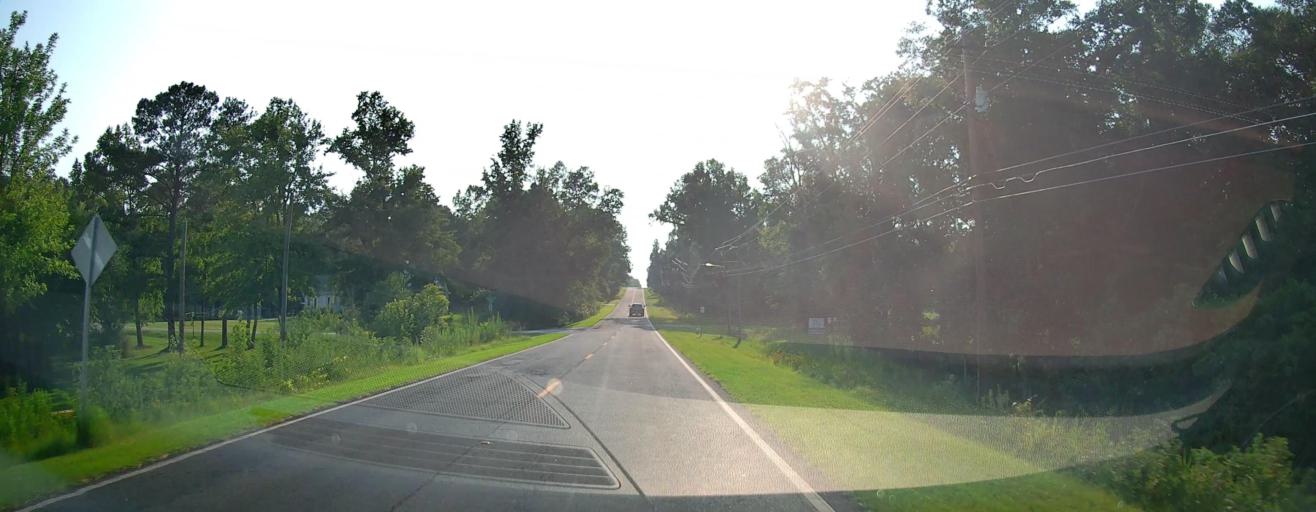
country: US
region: Georgia
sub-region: Bibb County
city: West Point
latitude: 32.8315
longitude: -83.7985
